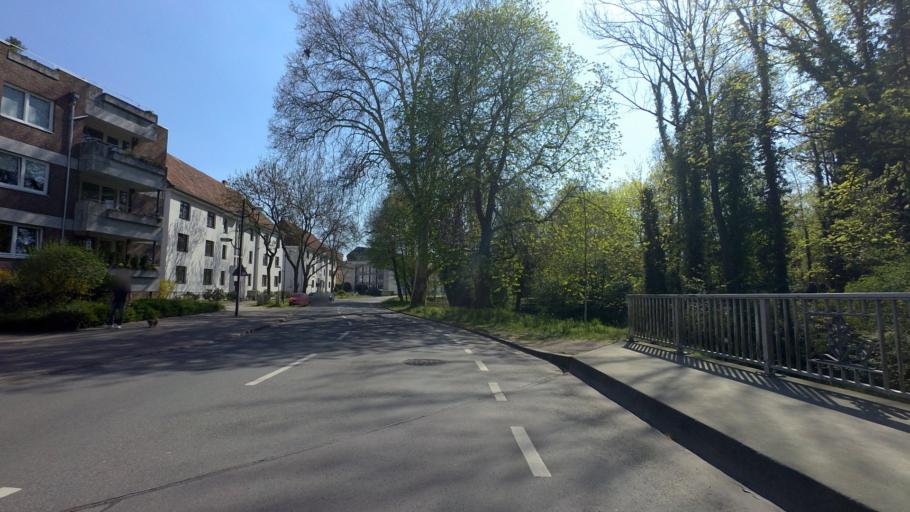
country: DE
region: Lower Saxony
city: Celle
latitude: 52.6218
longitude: 10.0864
